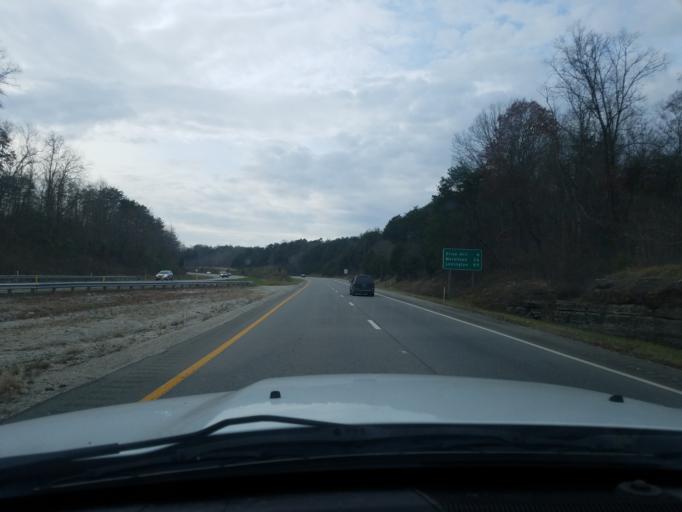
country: US
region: Kentucky
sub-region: Carter County
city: Olive Hill
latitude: 38.3262
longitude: -83.1292
